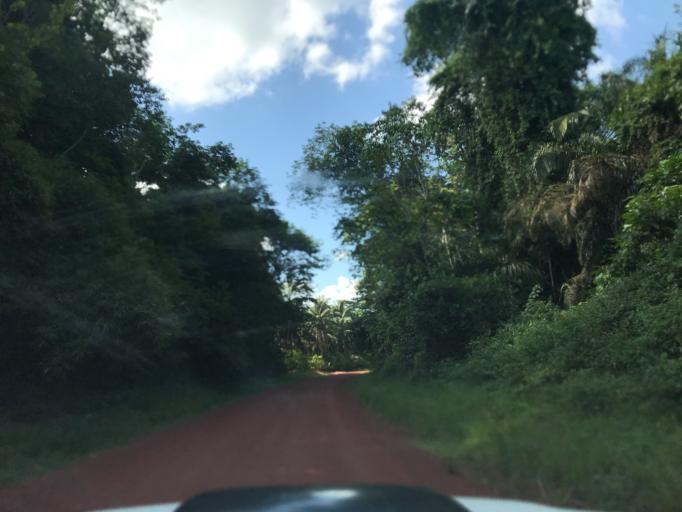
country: CD
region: Eastern Province
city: Kisangani
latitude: 1.2280
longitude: 25.2683
